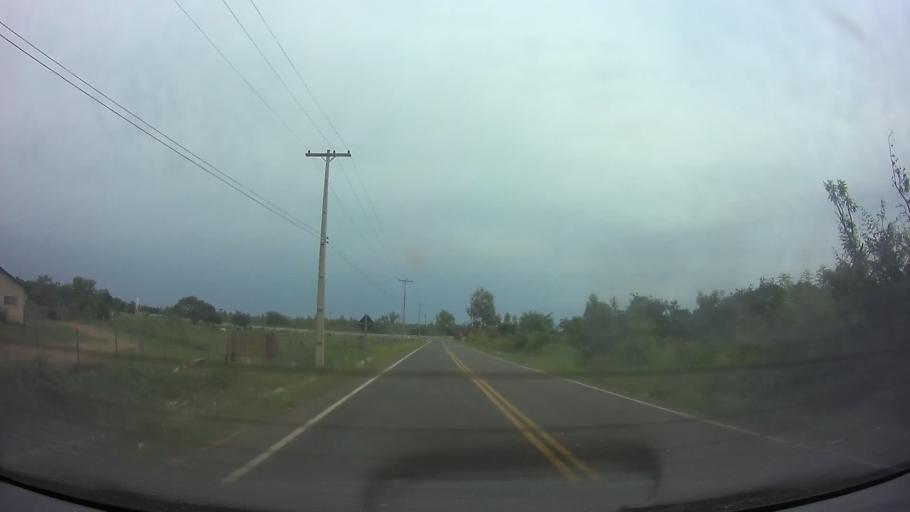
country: PY
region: Central
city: Limpio
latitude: -25.2128
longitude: -57.4818
